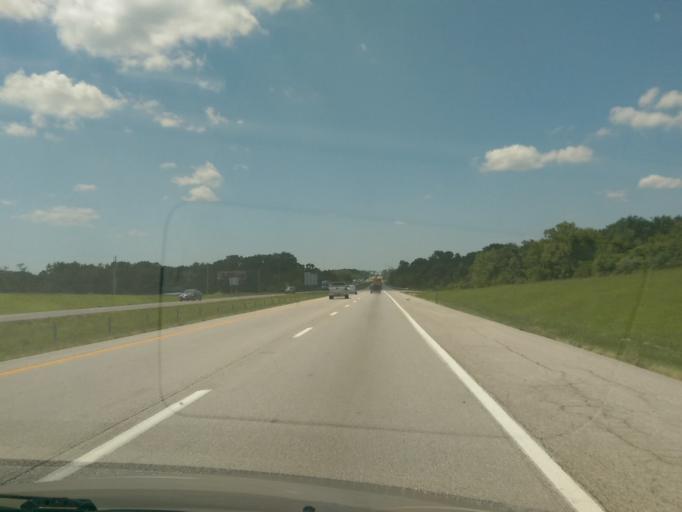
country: US
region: Missouri
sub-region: Cooper County
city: Boonville
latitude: 38.9377
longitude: -92.6923
